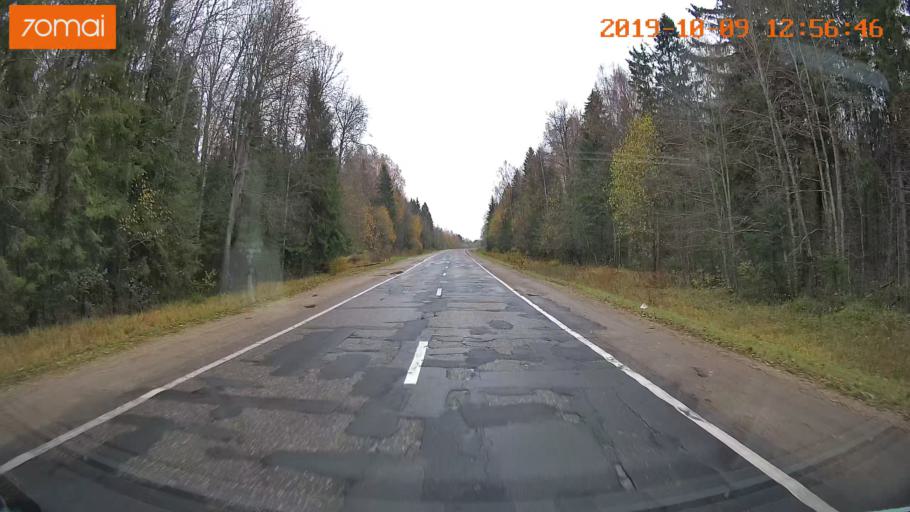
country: RU
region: Jaroslavl
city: Prechistoye
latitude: 58.3942
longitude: 40.4219
